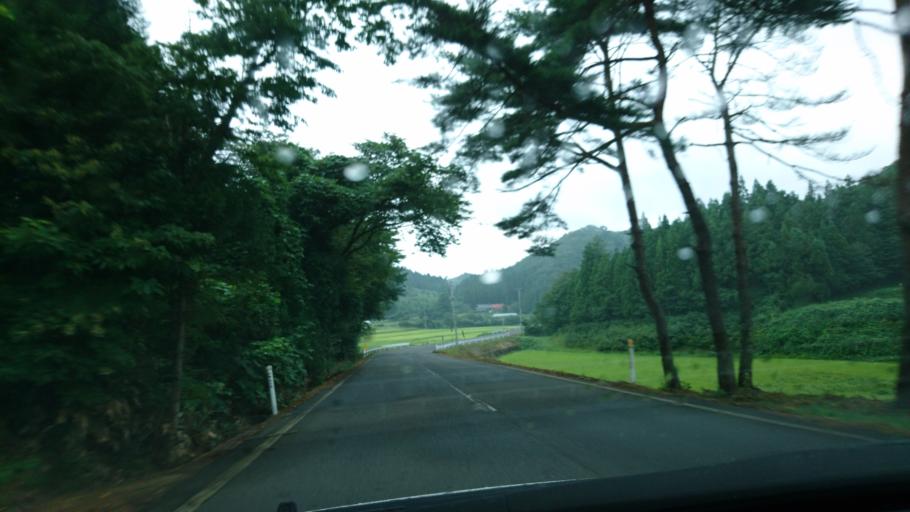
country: JP
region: Iwate
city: Ichinoseki
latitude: 38.8862
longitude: 140.9784
